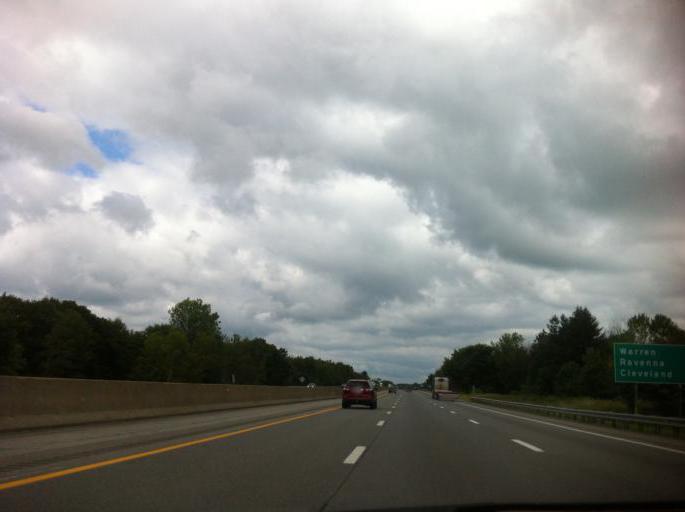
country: US
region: Ohio
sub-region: Trumbull County
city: Lordstown
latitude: 41.1606
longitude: -80.9031
